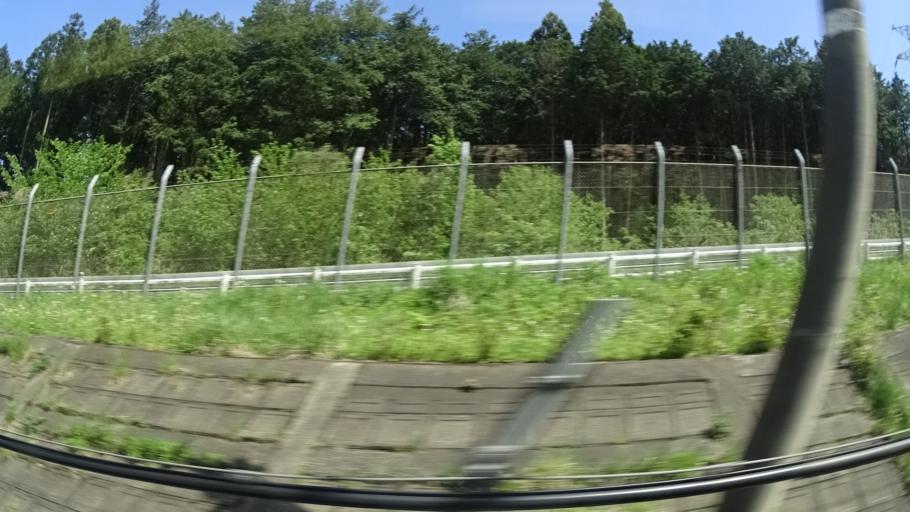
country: JP
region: Tochigi
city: Yaita
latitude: 36.7655
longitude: 139.9458
